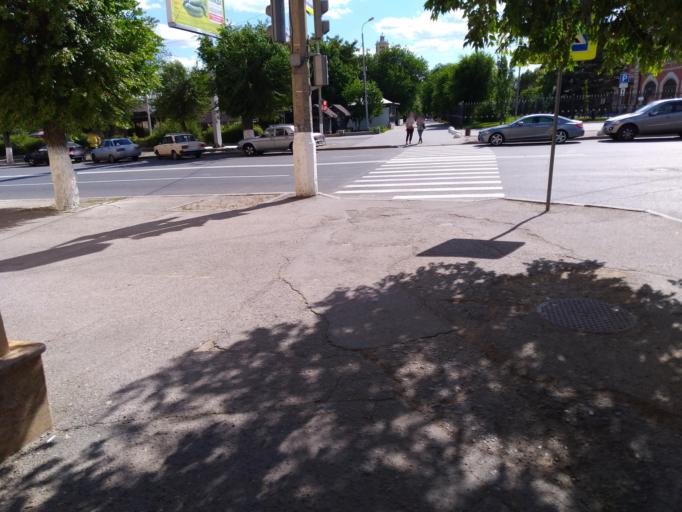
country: RU
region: Volgograd
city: Volgograd
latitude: 48.7098
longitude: 44.5116
